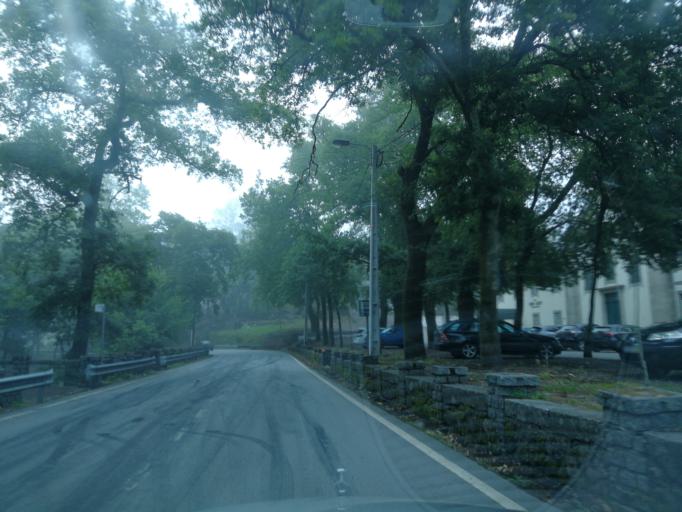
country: PT
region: Braga
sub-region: Braga
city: Braga
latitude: 41.5206
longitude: -8.3895
